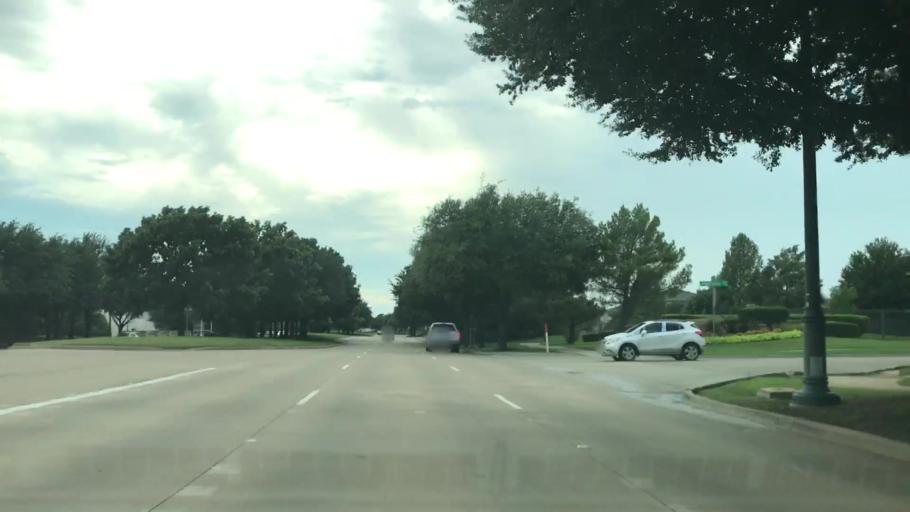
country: US
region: Texas
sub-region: Collin County
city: Frisco
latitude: 33.1092
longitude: -96.8100
